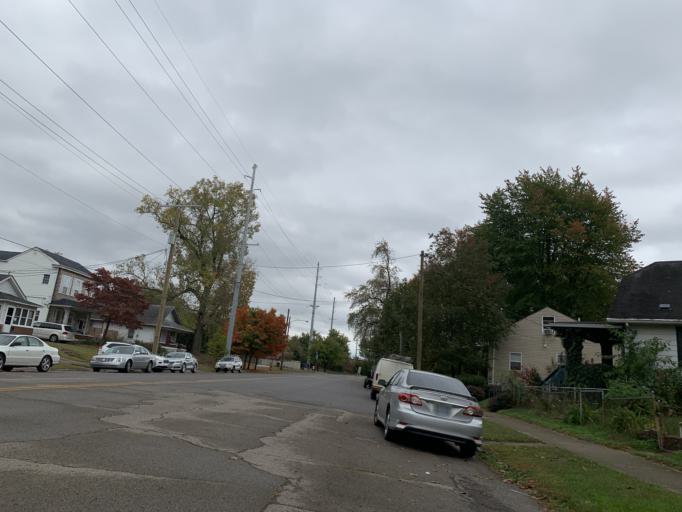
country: US
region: Indiana
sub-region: Floyd County
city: New Albany
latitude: 38.2751
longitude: -85.7985
